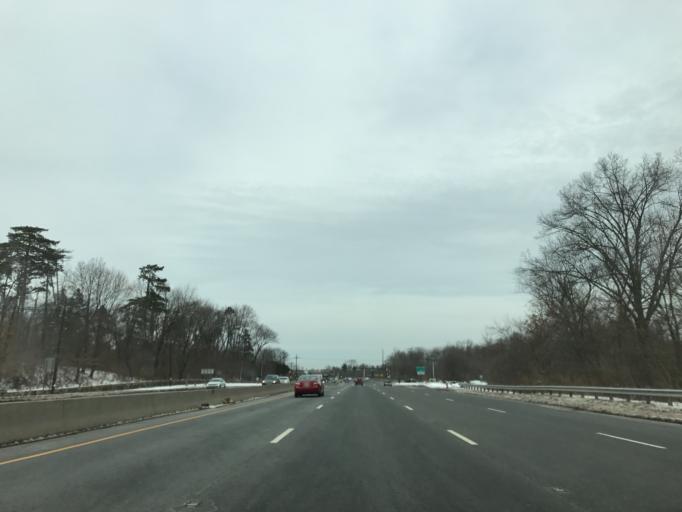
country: US
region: New Jersey
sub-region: Somerset County
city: Somerville
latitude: 40.5521
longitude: -74.6149
